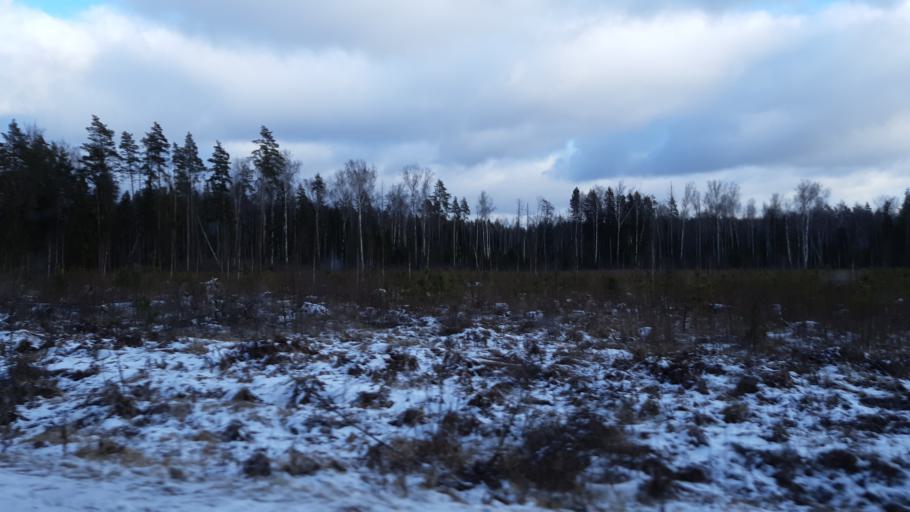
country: RU
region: Moskovskaya
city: Noginsk-9
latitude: 55.9693
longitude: 38.5369
